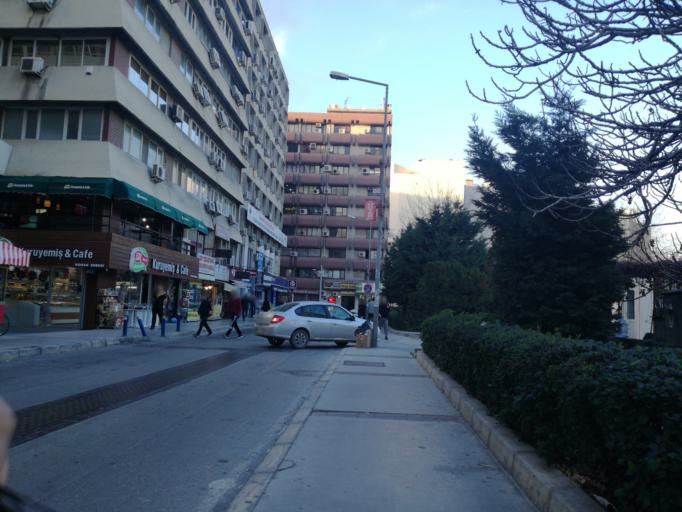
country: TR
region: Izmir
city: Izmir
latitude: 38.4207
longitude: 27.1309
